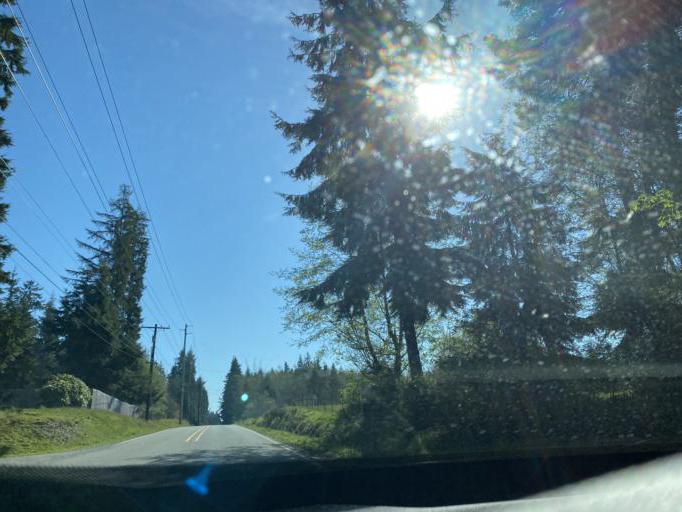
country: US
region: Washington
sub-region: Island County
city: Freeland
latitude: 48.0798
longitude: -122.5971
